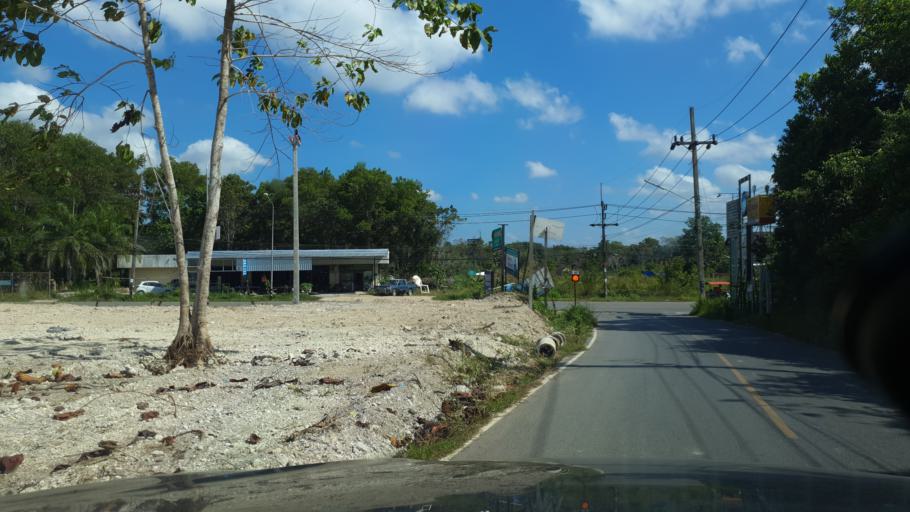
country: TH
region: Phangnga
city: Ban Ao Nang
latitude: 8.0343
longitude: 98.8580
